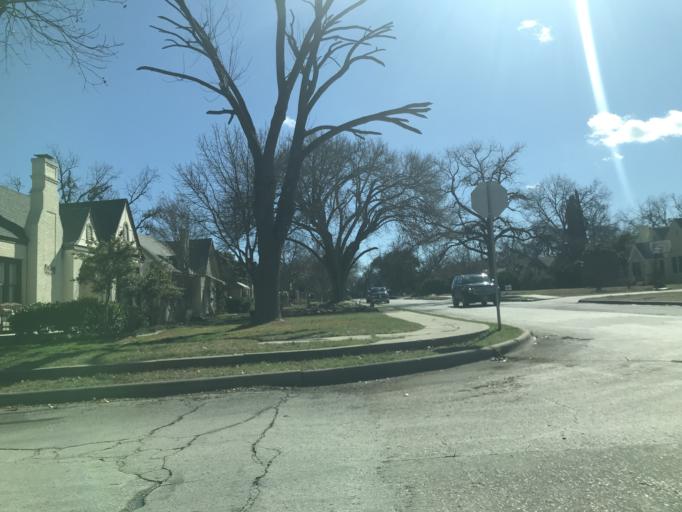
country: US
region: Texas
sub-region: Tom Green County
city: San Angelo
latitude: 31.4474
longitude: -100.4495
